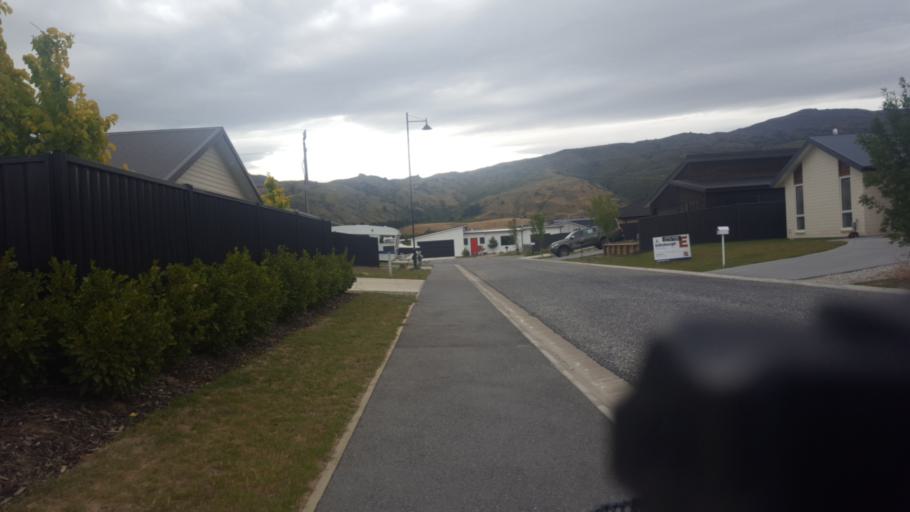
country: NZ
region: Otago
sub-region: Queenstown-Lakes District
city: Wanaka
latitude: -45.0477
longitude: 169.1784
